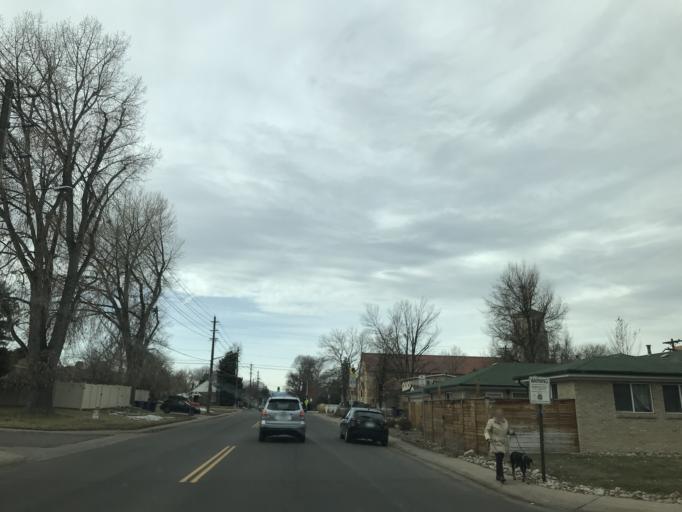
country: US
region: Colorado
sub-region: Arapahoe County
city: Glendale
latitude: 39.7293
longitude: -104.9269
